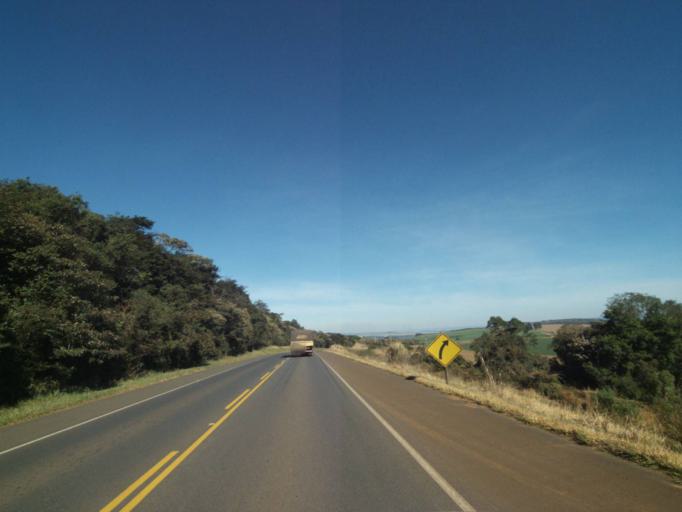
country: BR
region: Parana
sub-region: Tibagi
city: Tibagi
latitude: -24.3739
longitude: -50.3264
